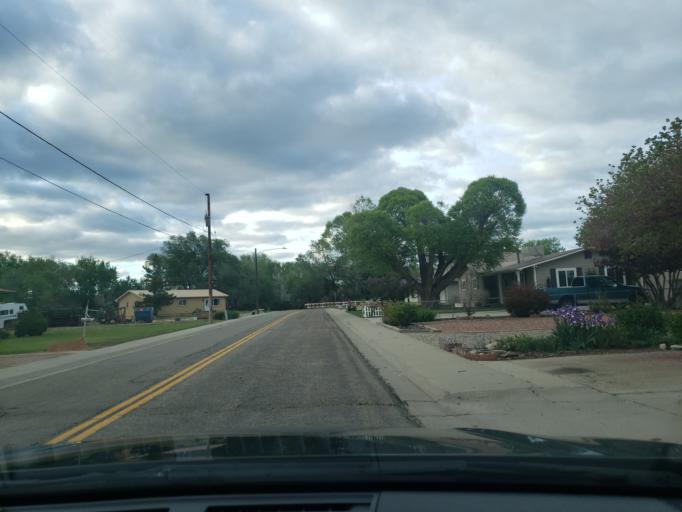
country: US
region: Colorado
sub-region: Mesa County
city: Fruita
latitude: 39.1651
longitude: -108.7325
